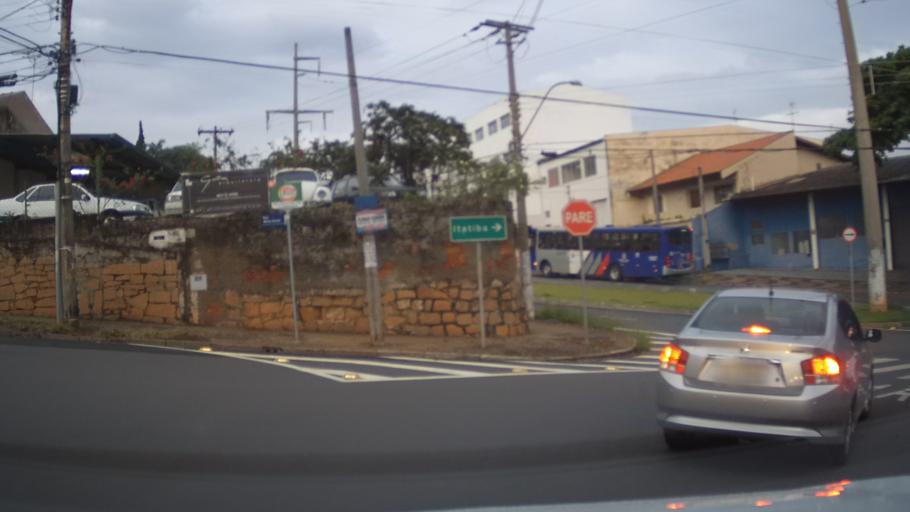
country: BR
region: Sao Paulo
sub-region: Valinhos
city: Valinhos
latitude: -22.9666
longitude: -46.9910
